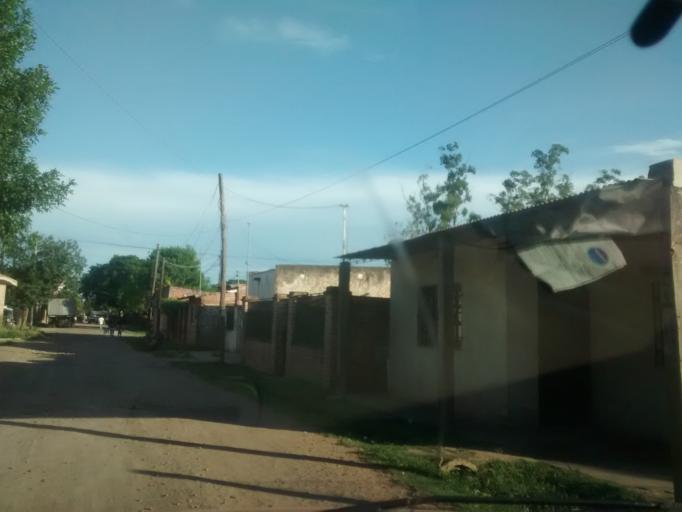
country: AR
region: Chaco
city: Fontana
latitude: -27.4323
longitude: -58.9985
